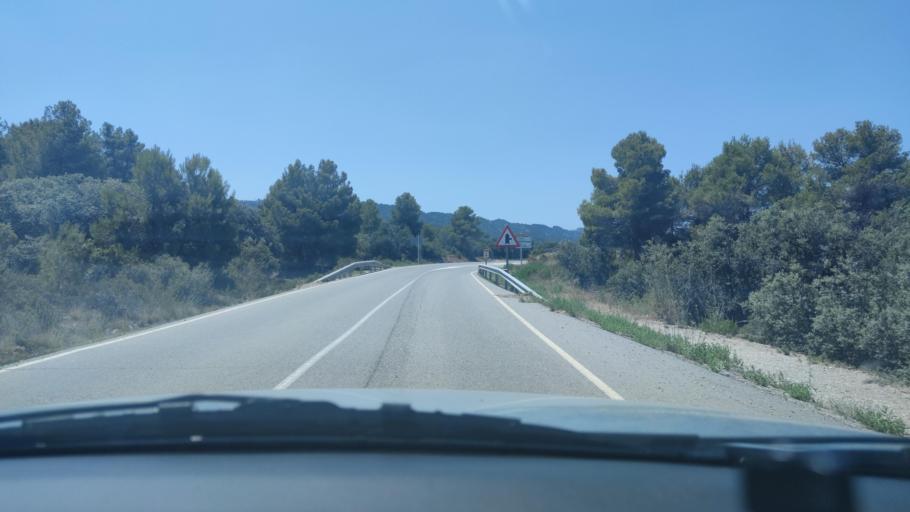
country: ES
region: Catalonia
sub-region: Provincia de Tarragona
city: Vilanova de Prades
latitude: 41.3693
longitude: 0.9287
